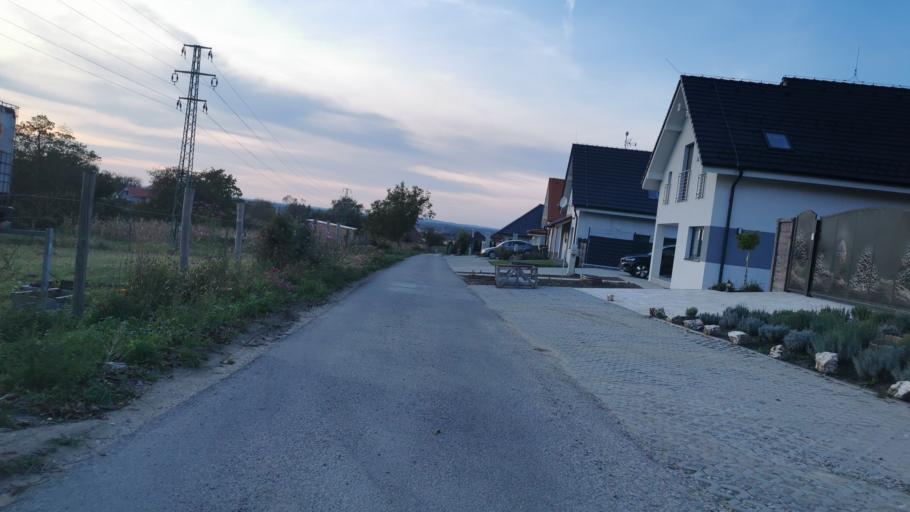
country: SK
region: Trnavsky
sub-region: Okres Skalica
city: Skalica
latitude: 48.8261
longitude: 17.2273
